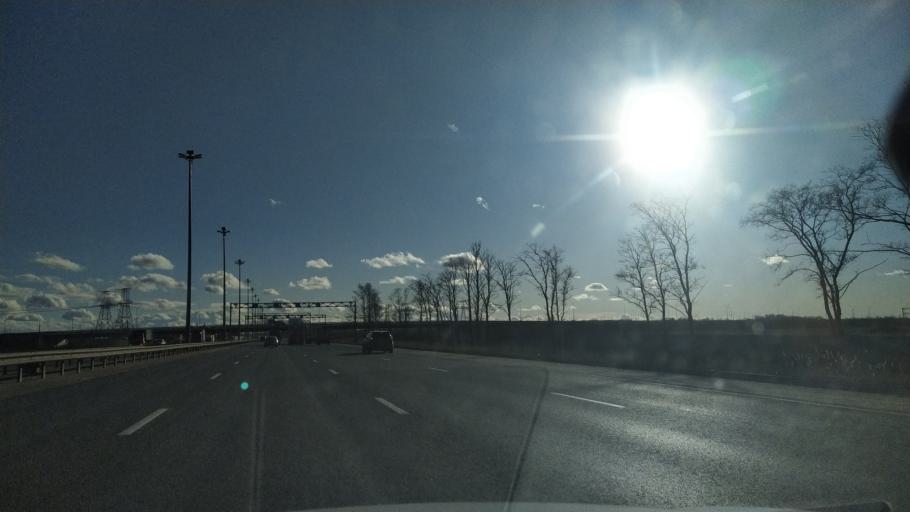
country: RU
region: St.-Petersburg
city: Aleksandrovskaya
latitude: 59.7475
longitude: 30.3127
